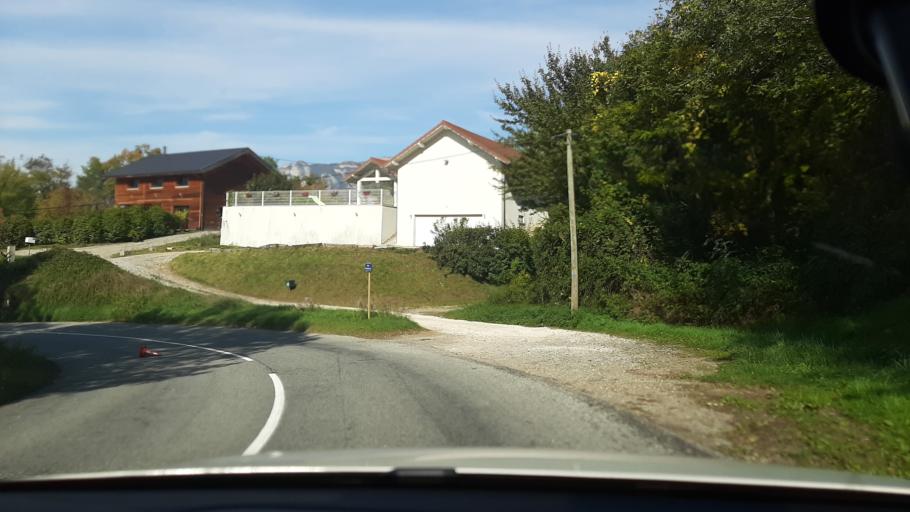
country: FR
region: Rhone-Alpes
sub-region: Departement de l'Isere
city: Pontcharra
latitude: 45.4561
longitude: 6.0503
